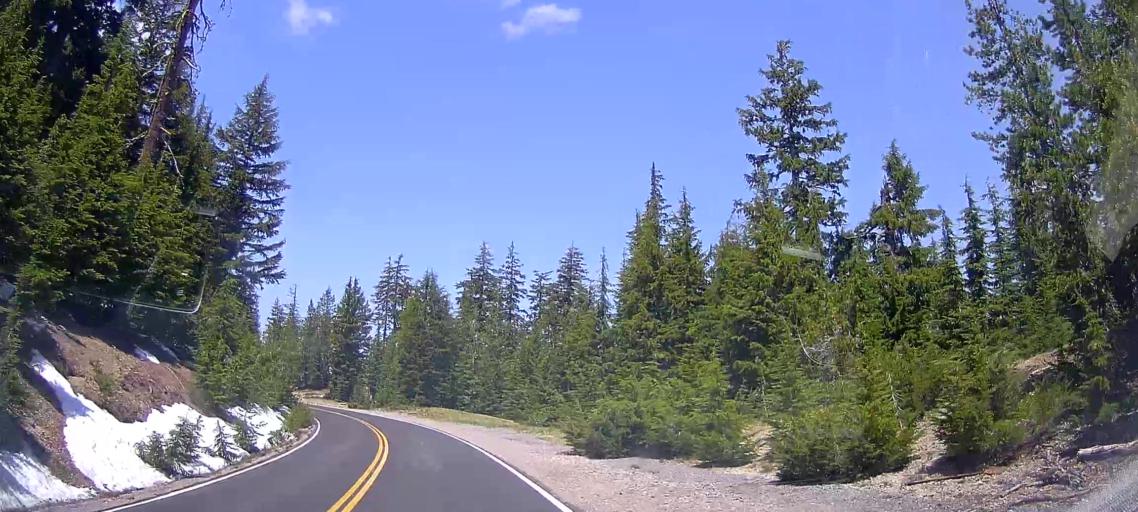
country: US
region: Oregon
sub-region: Jackson County
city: Shady Cove
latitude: 42.9811
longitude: -122.1087
